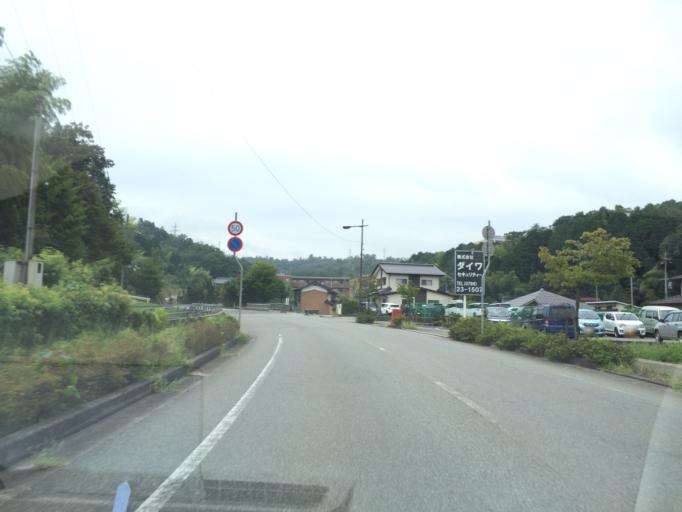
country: JP
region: Hyogo
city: Toyooka
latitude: 35.5315
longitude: 134.8077
